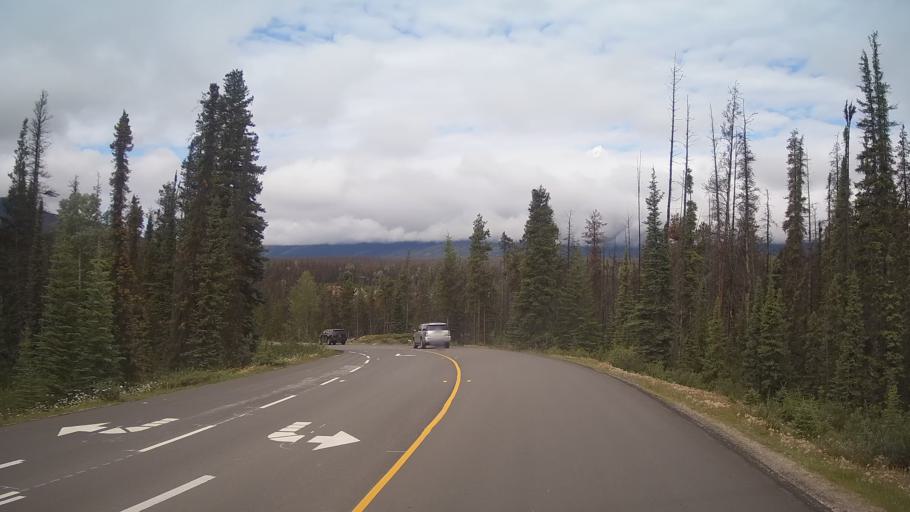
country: CA
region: Alberta
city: Jasper Park Lodge
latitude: 52.6690
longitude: -117.8824
